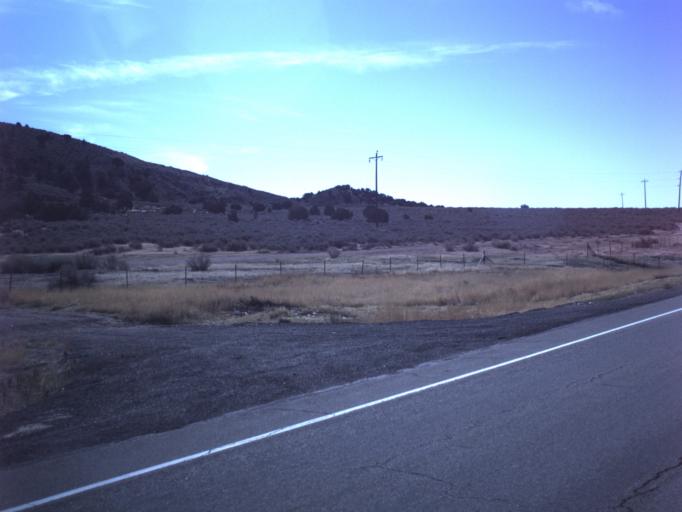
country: US
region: Utah
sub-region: Sanpete County
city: Gunnison
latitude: 39.4078
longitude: -111.9265
